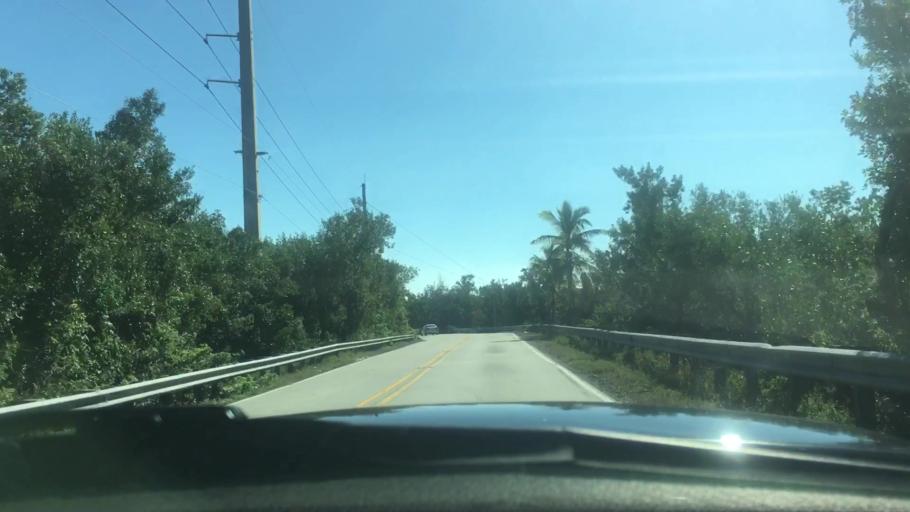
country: US
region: Florida
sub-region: Monroe County
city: North Key Largo
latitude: 25.2932
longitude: -80.3818
